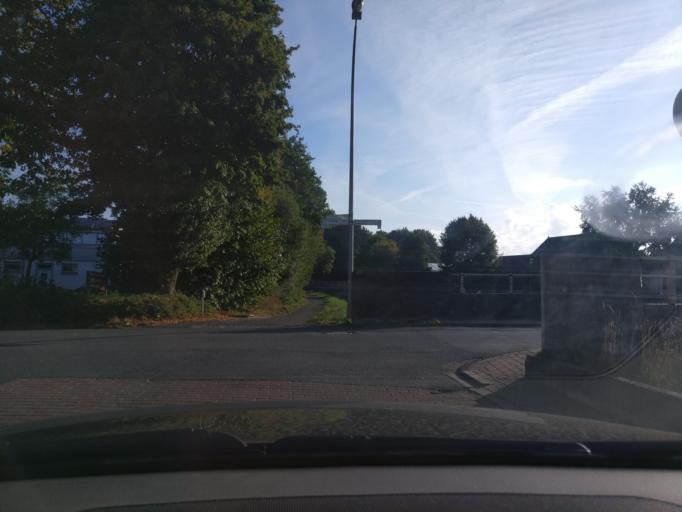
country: DE
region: Lower Saxony
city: Melle
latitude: 52.2134
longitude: 8.2718
